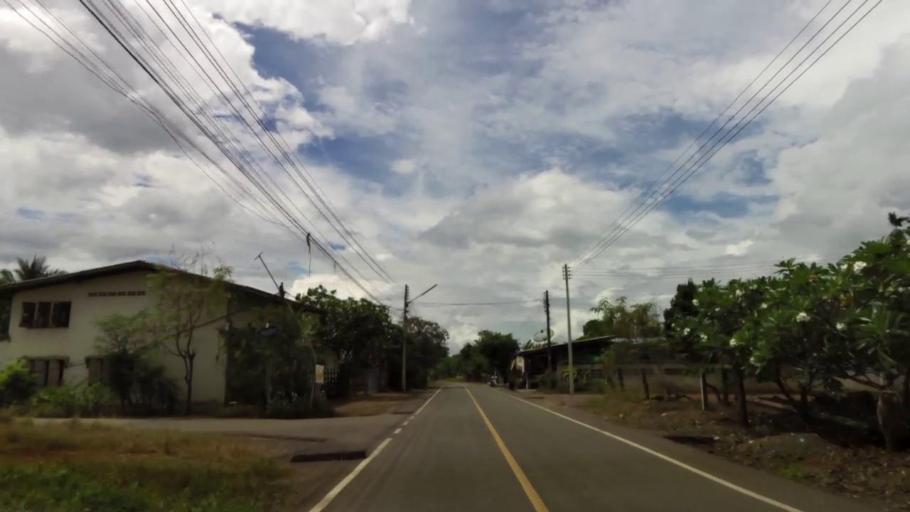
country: TH
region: Nakhon Sawan
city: Phai Sali
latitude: 15.6023
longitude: 100.6502
